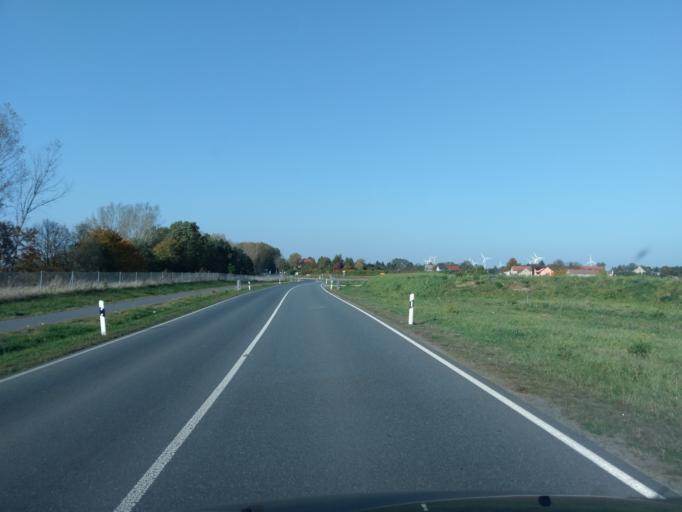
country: DE
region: Brandenburg
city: Muhlberg
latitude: 51.4435
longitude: 13.2261
